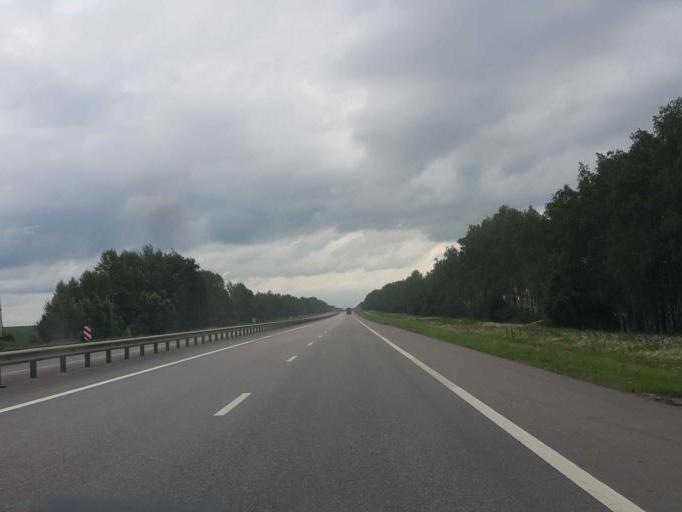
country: RU
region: Tambov
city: Selezni
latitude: 52.8108
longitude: 40.9542
